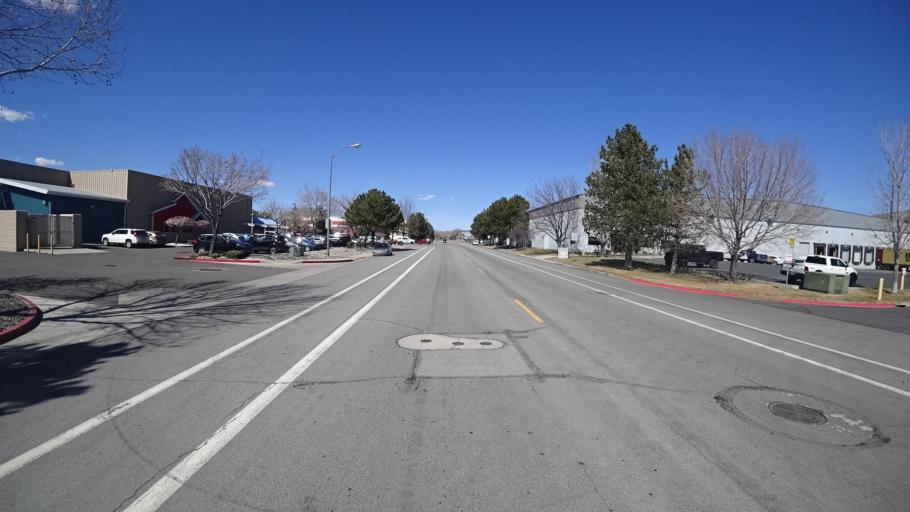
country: US
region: Nevada
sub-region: Washoe County
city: Sparks
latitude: 39.5326
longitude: -119.7112
